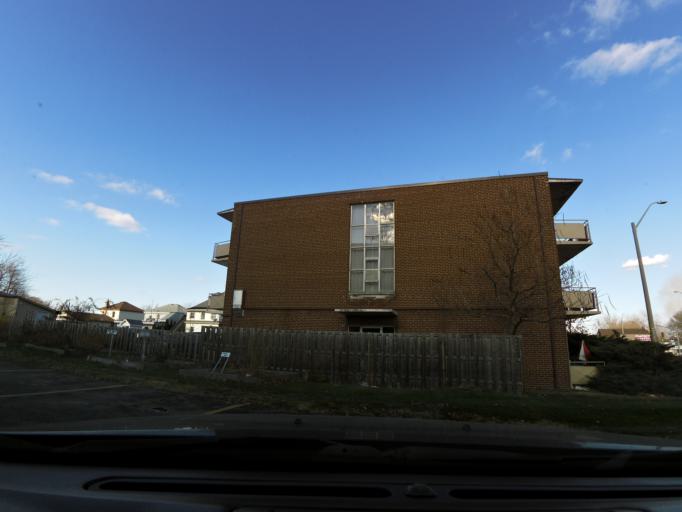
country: CA
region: Ontario
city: Hamilton
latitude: 43.2320
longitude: -79.8586
